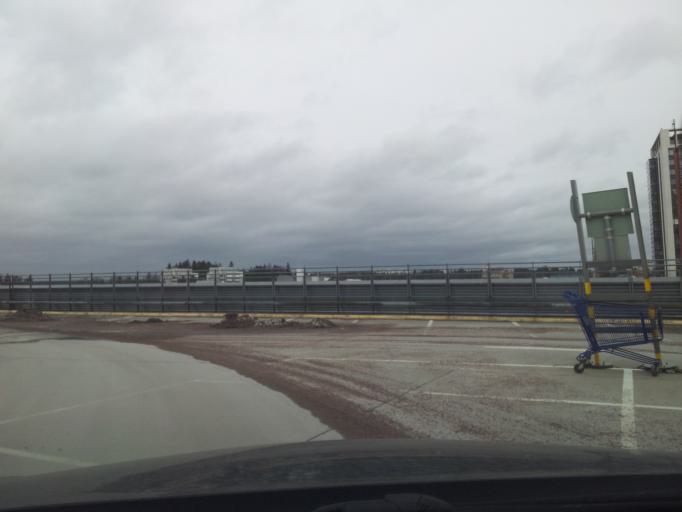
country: FI
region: Uusimaa
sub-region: Helsinki
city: Kilo
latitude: 60.2189
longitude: 24.8133
